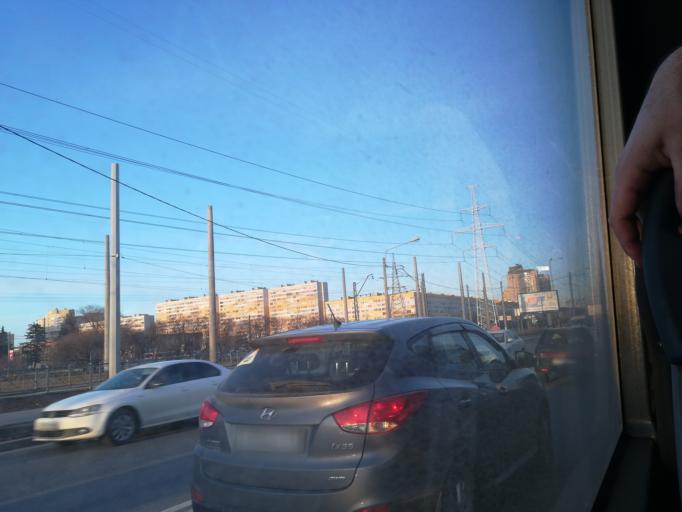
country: RU
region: St.-Petersburg
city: Uritsk
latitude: 59.8463
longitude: 30.1732
